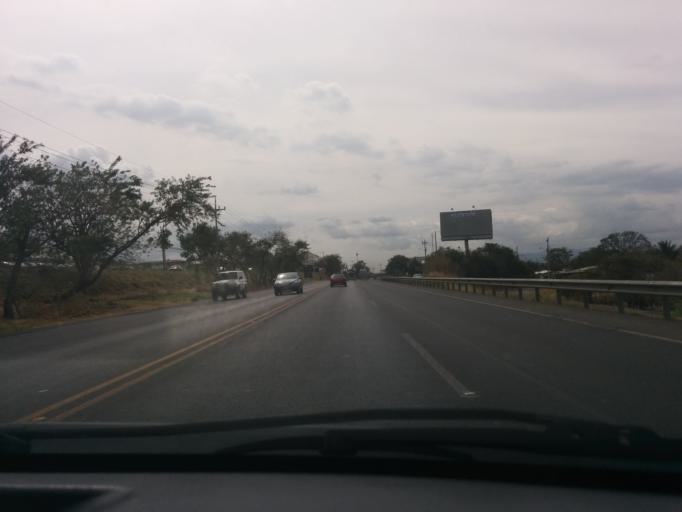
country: CR
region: Alajuela
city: Alajuela
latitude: 9.9990
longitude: -84.2090
